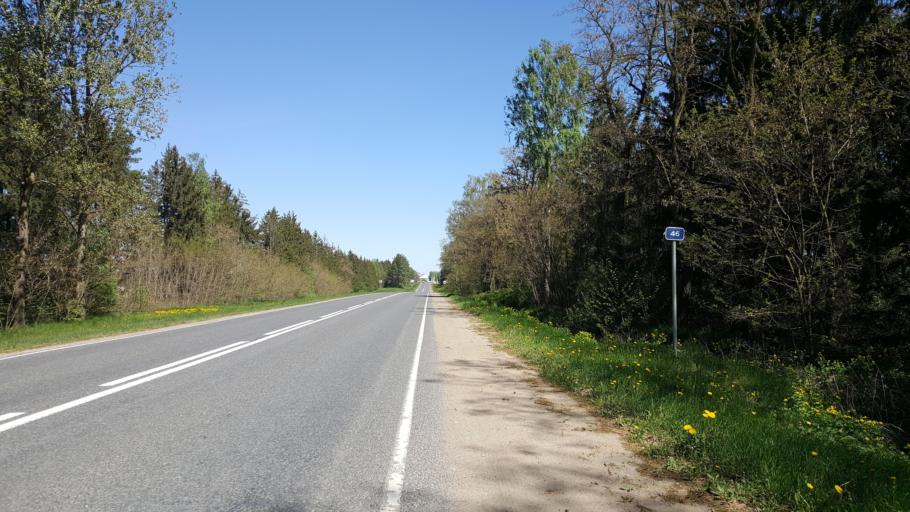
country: BY
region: Brest
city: Kamyanyuki
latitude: 52.4798
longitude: 23.7795
